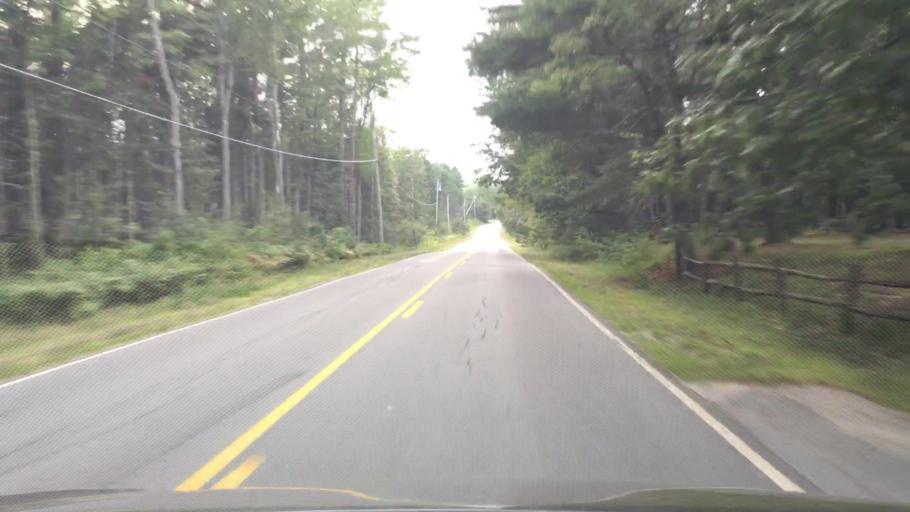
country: US
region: Maine
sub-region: Hancock County
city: Penobscot
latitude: 44.4506
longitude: -68.6956
